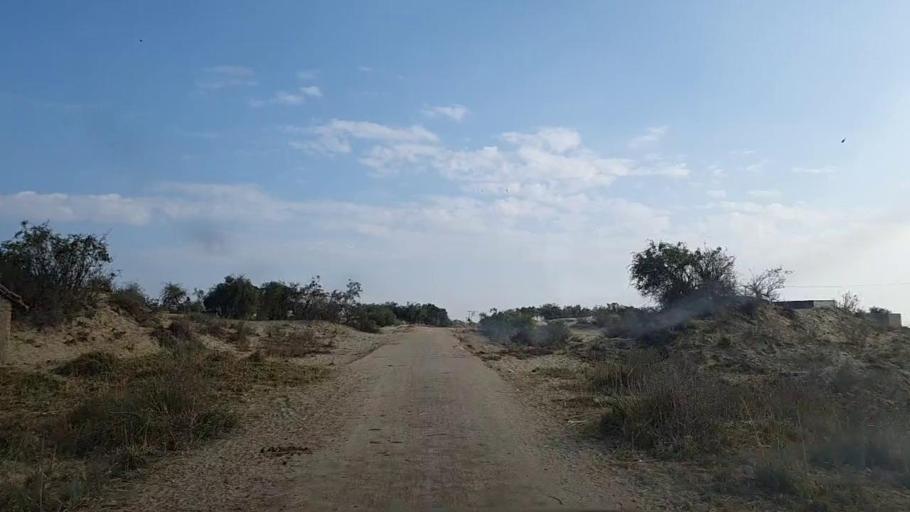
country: PK
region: Sindh
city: Sanghar
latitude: 26.2036
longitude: 69.0258
